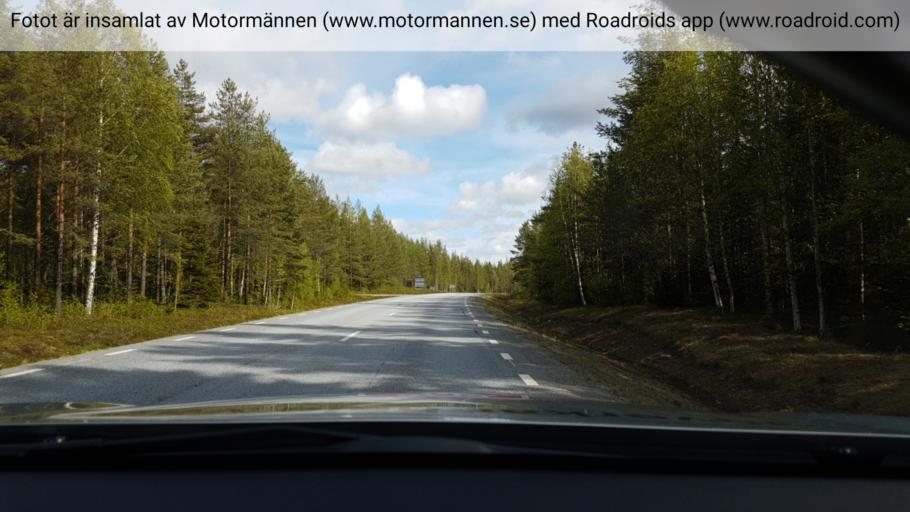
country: SE
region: Vaesterbotten
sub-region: Lycksele Kommun
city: Lycksele
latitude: 64.0683
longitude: 18.4316
